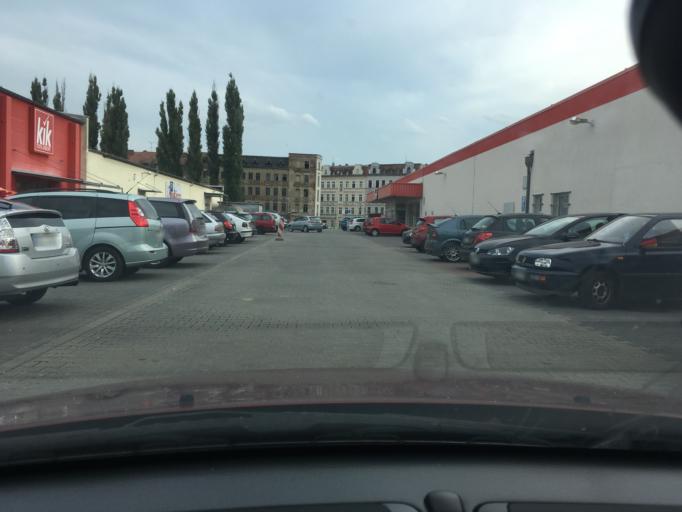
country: DE
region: Saxony
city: Goerlitz
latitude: 51.1529
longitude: 14.9652
